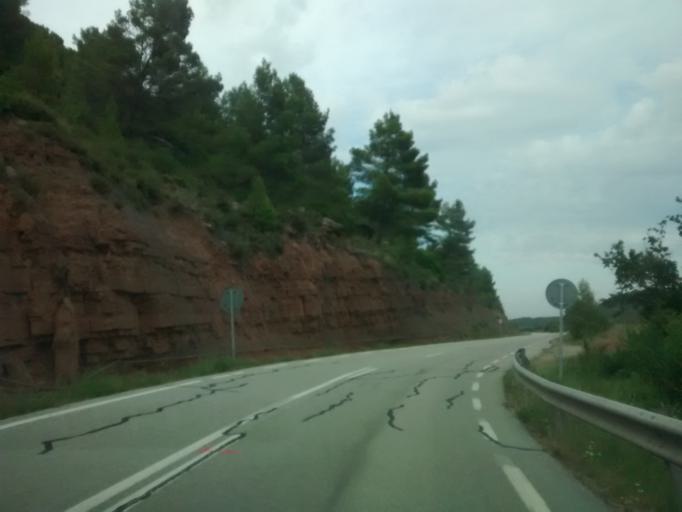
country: ES
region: Catalonia
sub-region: Provincia de Barcelona
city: Fonollosa
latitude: 41.7616
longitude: 1.6942
